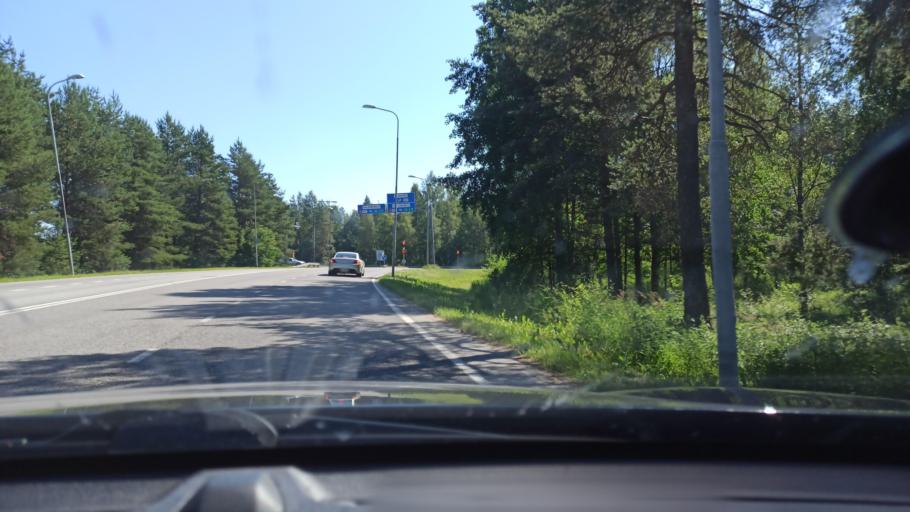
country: FI
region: Northern Ostrobothnia
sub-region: Oulu
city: Oulu
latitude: 65.0392
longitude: 25.4671
